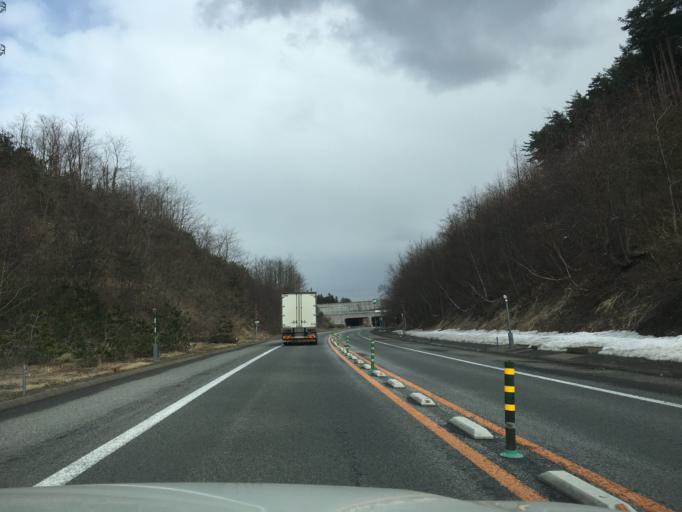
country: JP
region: Aomori
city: Aomori Shi
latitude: 40.8038
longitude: 140.6891
